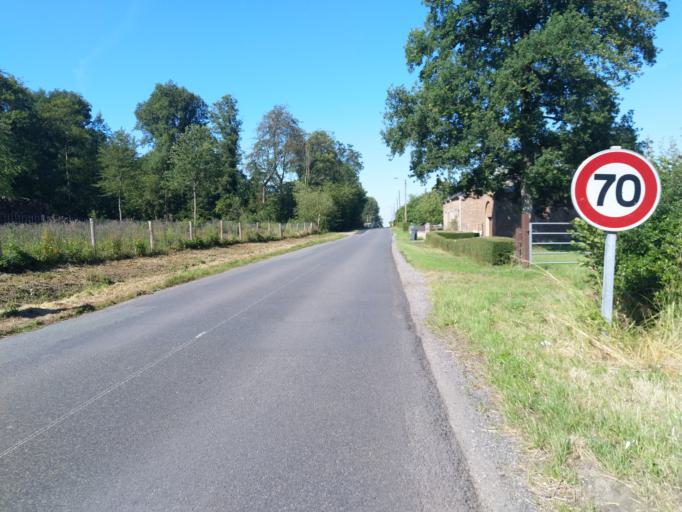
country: FR
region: Nord-Pas-de-Calais
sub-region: Departement du Nord
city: La Longueville
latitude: 50.3187
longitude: 3.8730
